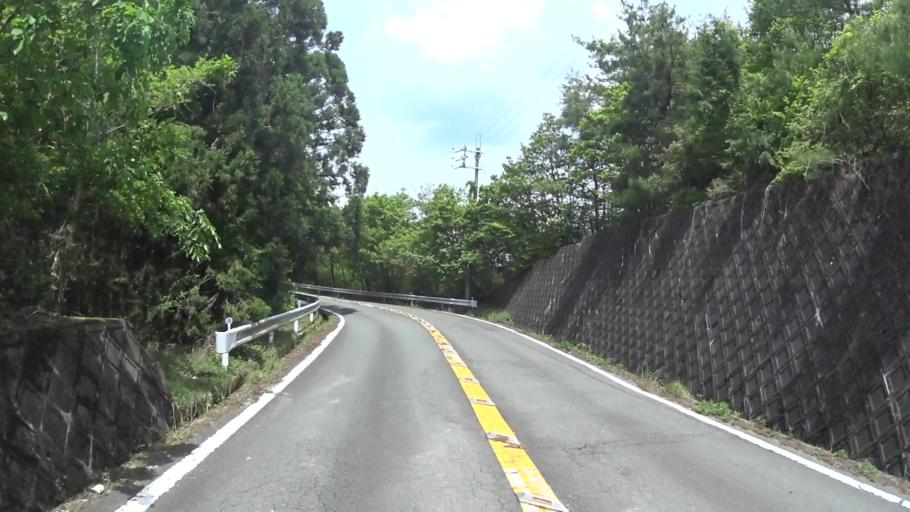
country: JP
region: Kyoto
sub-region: Kyoto-shi
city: Kamigyo-ku
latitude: 35.0630
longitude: 135.7241
